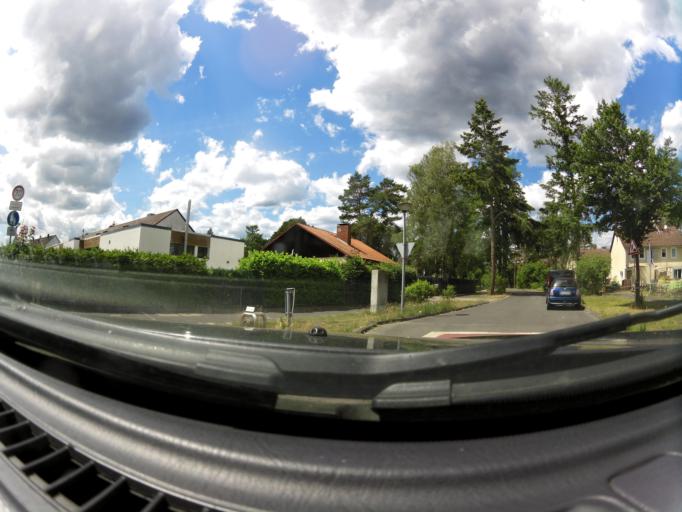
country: DE
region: Lower Saxony
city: Celle
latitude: 52.6324
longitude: 10.0538
